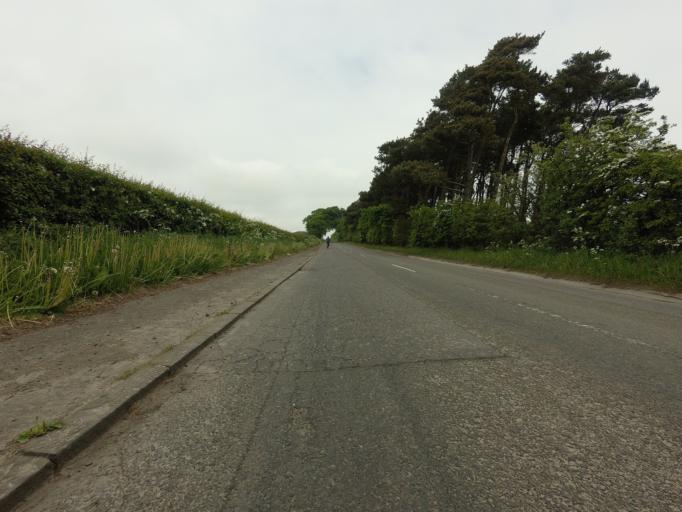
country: GB
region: Scotland
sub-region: Fife
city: Townhill
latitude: 56.0953
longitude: -3.4427
